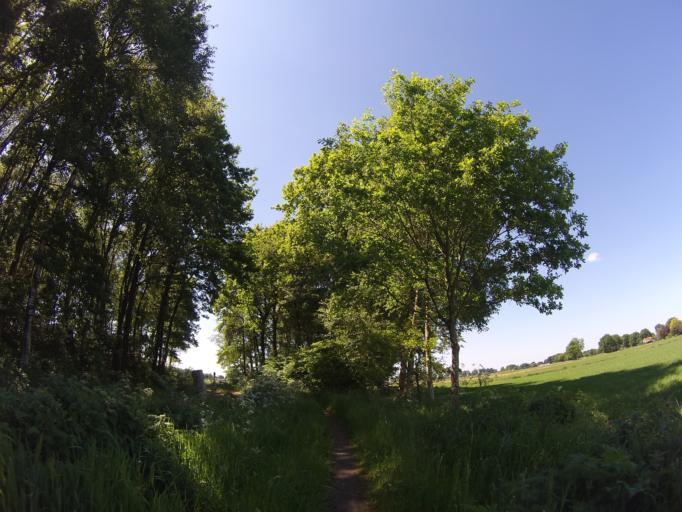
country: NL
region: Drenthe
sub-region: Gemeente Coevorden
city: Dalen
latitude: 52.7635
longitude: 6.6265
